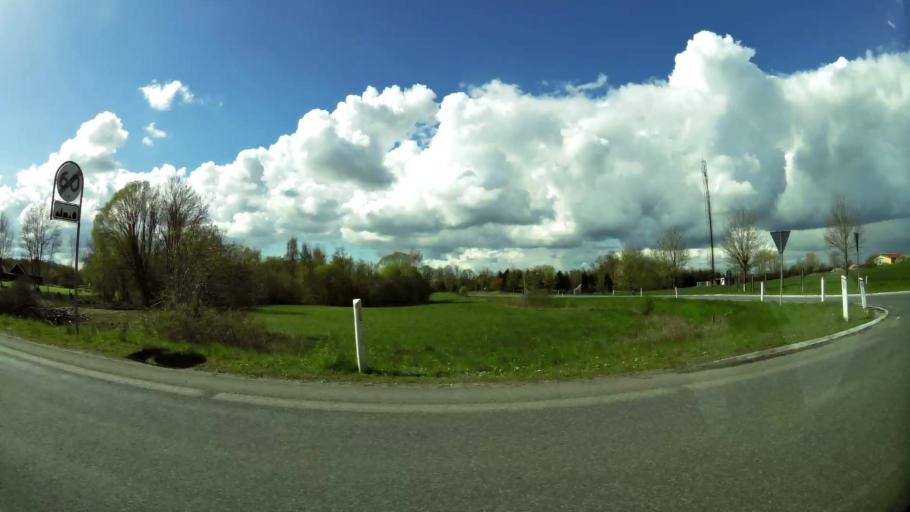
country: DK
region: South Denmark
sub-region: Middelfart Kommune
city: Brenderup
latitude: 55.4853
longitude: 9.9755
